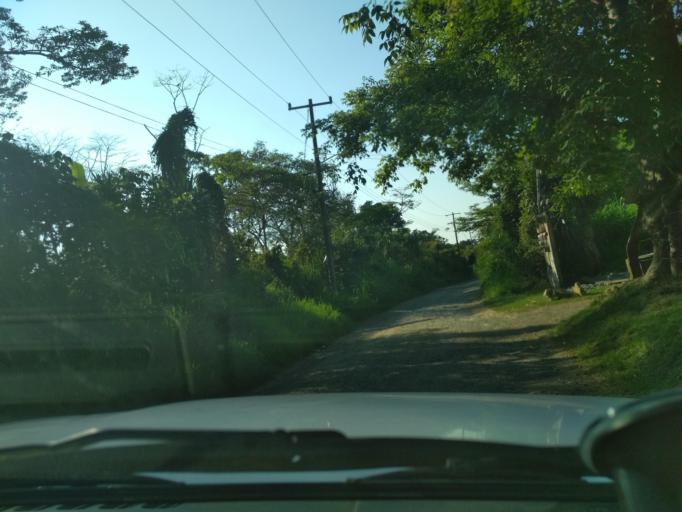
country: MX
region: Veracruz
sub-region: Fortin
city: Fraccionamiento Villas de la Llave
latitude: 18.9219
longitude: -96.9911
